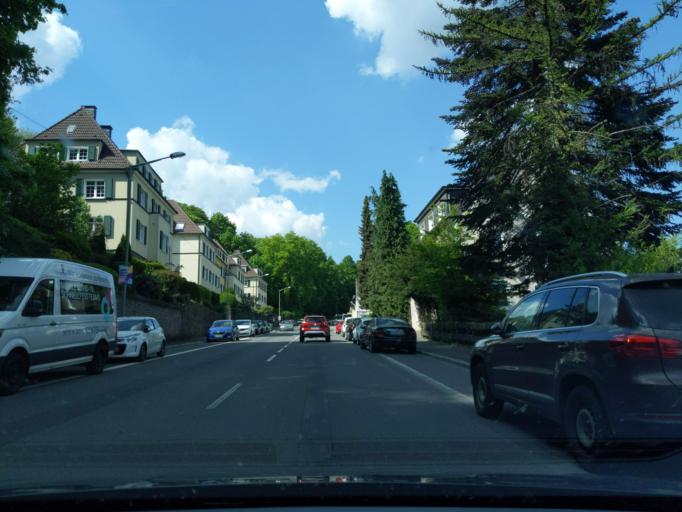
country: DE
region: North Rhine-Westphalia
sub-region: Regierungsbezirk Koln
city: Gummersbach
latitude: 51.0209
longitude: 7.5716
